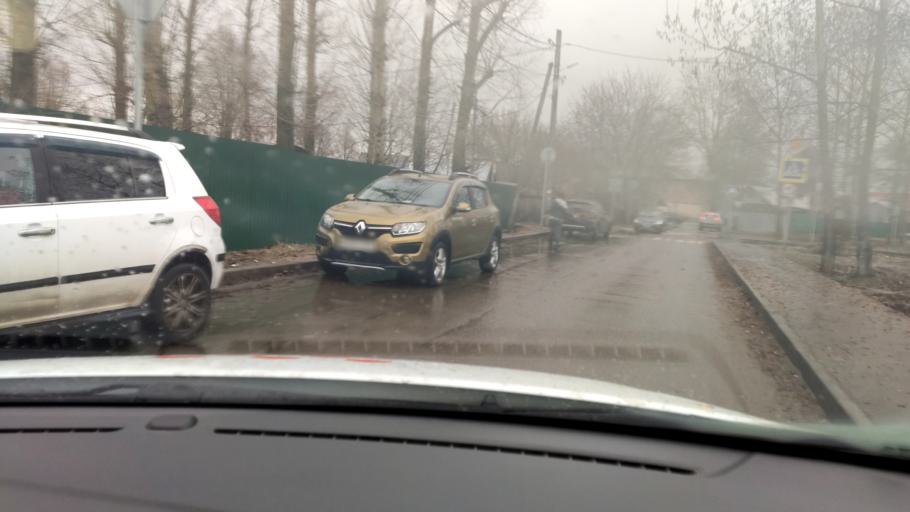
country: RU
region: Tatarstan
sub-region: Gorod Kazan'
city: Kazan
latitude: 55.7063
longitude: 49.1454
